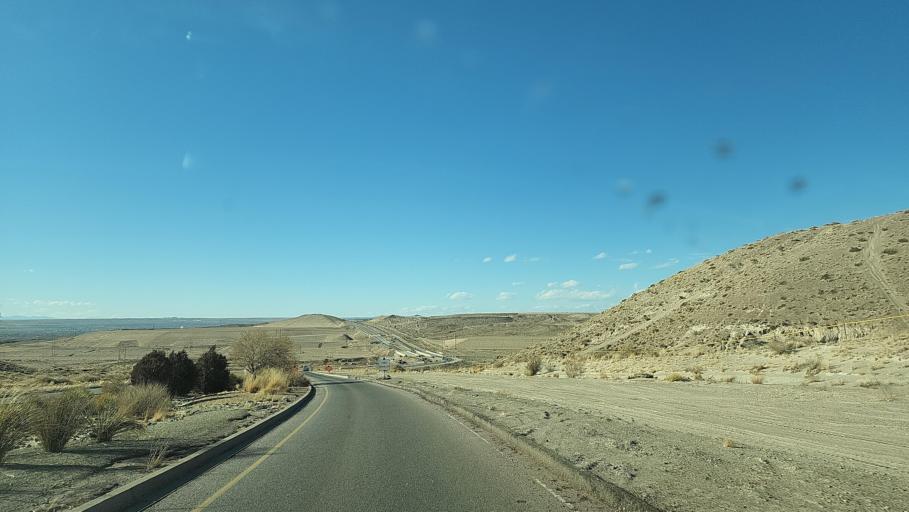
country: US
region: New Mexico
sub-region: Bernalillo County
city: South Valley
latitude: 35.0052
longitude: -106.6227
